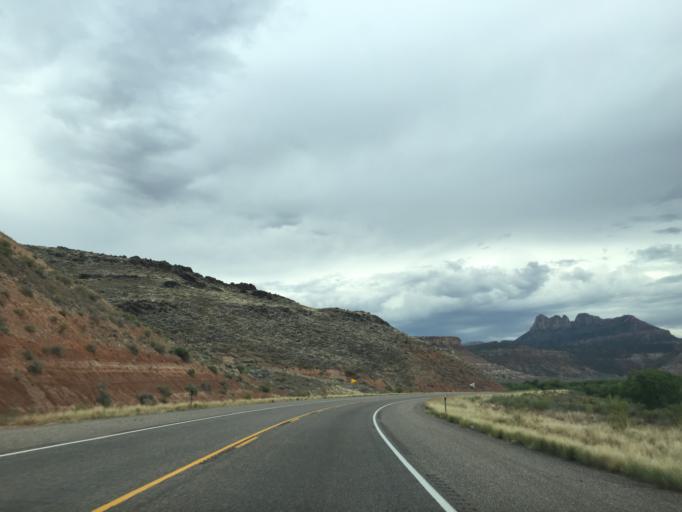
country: US
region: Utah
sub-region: Washington County
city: LaVerkin
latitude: 37.1777
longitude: -113.1162
